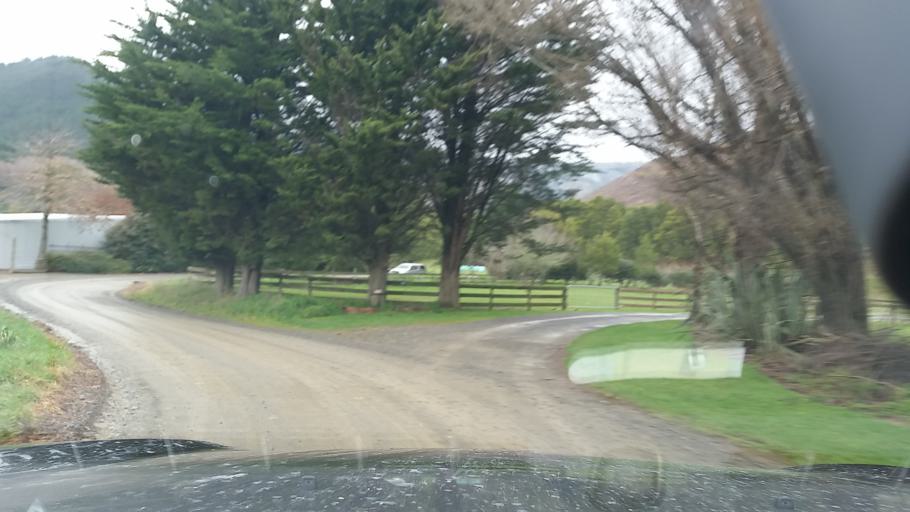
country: NZ
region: Marlborough
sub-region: Marlborough District
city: Picton
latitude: -41.3034
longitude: 173.6631
